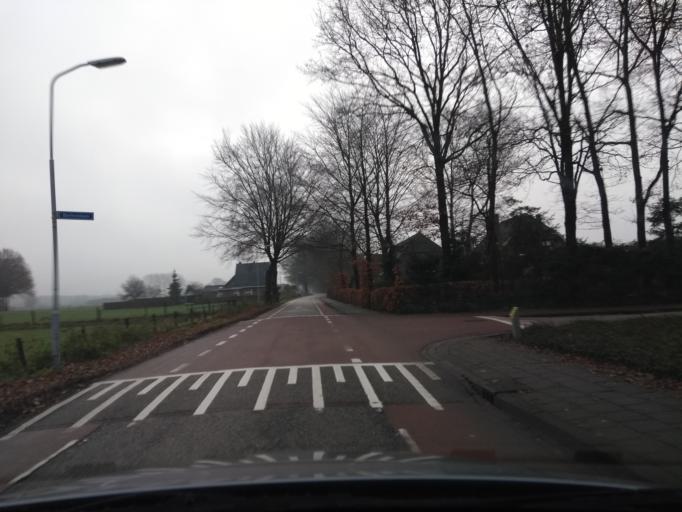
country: NL
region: Gelderland
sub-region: Gemeente Bronckhorst
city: Hengelo
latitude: 52.0494
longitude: 6.3167
